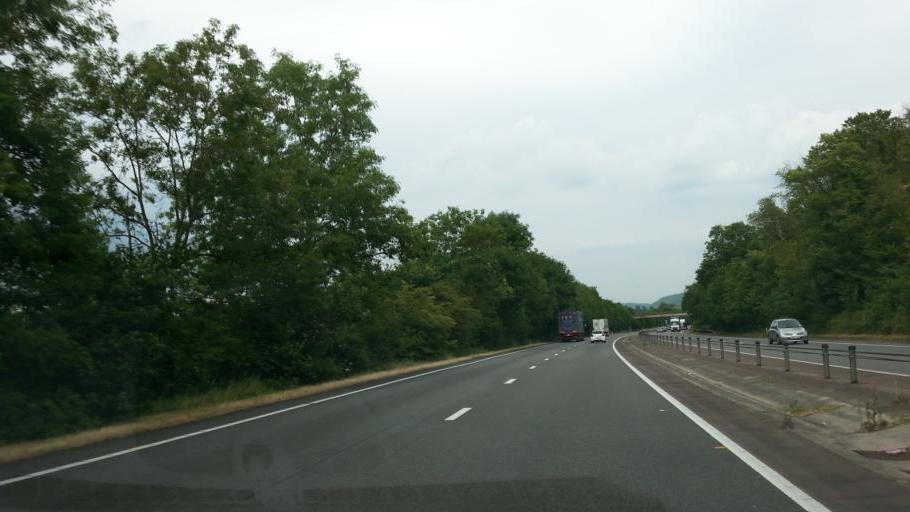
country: GB
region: Wales
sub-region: Monmouthshire
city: Mitchel Troy
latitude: 51.7889
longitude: -2.7666
